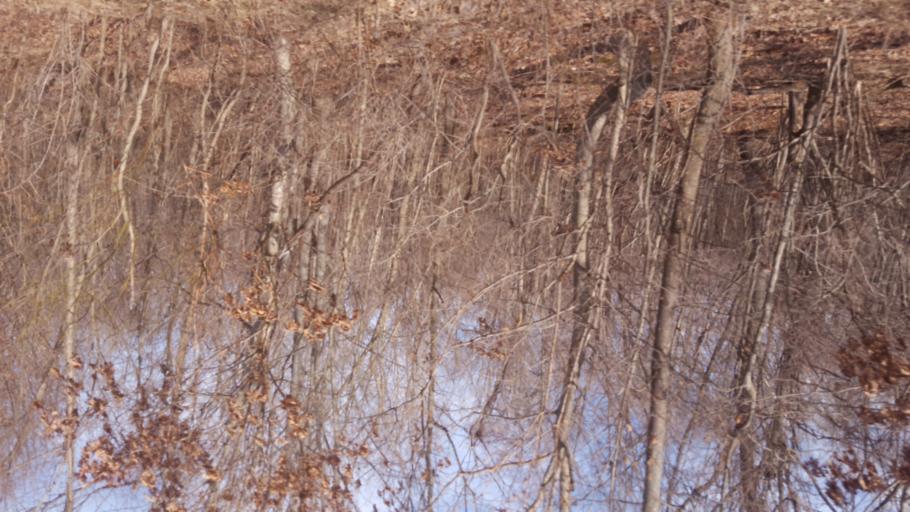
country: US
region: Ohio
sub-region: Ashland County
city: Loudonville
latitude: 40.5656
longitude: -82.3425
